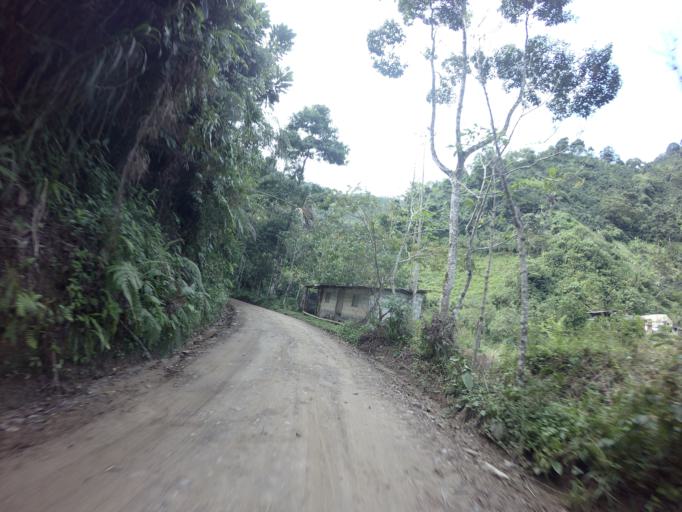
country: CO
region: Caldas
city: Marquetalia
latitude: 5.3360
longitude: -75.0516
